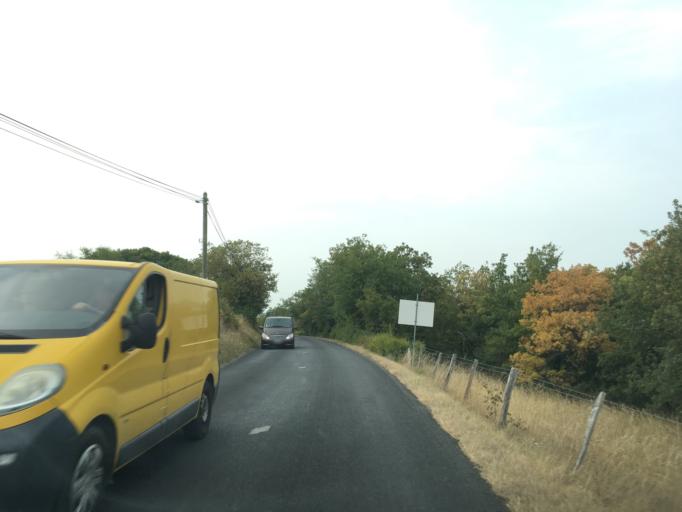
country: FR
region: Midi-Pyrenees
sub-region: Departement du Lot
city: Souillac
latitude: 44.8315
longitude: 1.5656
